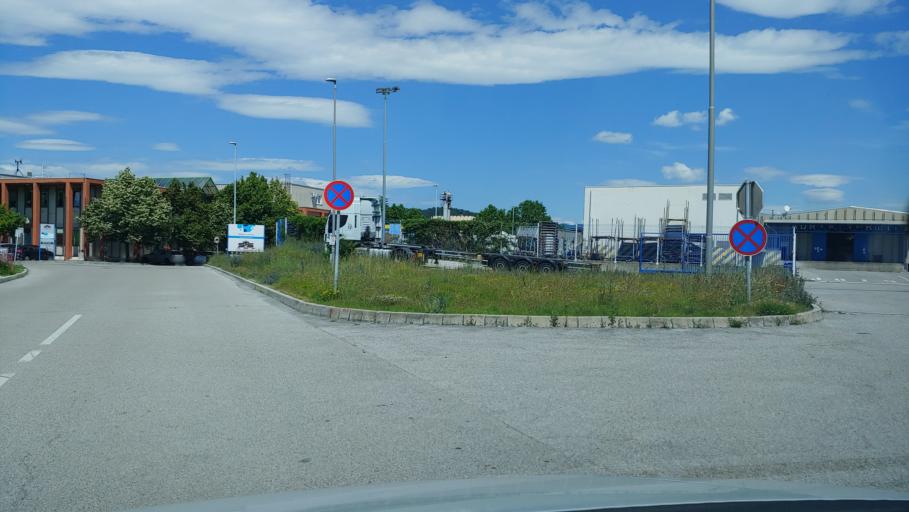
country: SI
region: Sezana
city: Sezana
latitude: 45.7013
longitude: 13.8467
